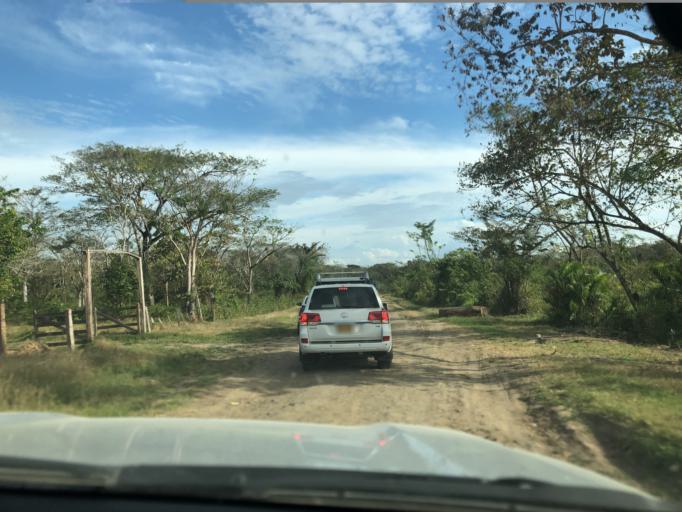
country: CR
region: Alajuela
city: San Jose
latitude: 11.1175
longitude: -85.2841
